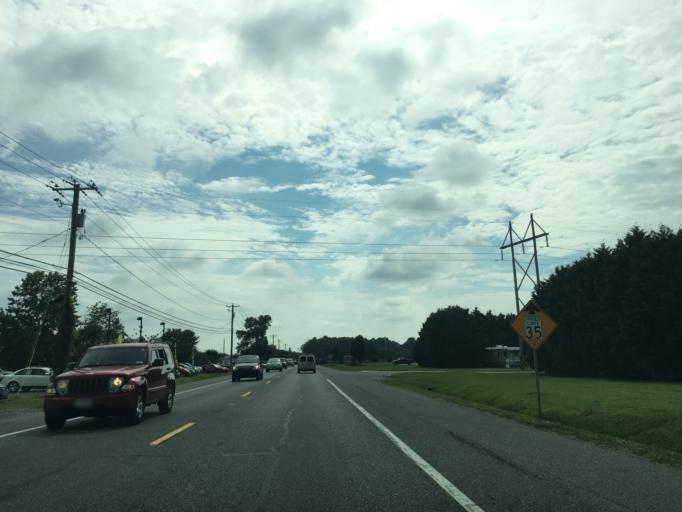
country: US
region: Delaware
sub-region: Sussex County
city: Millsboro
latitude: 38.5503
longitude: -75.2287
